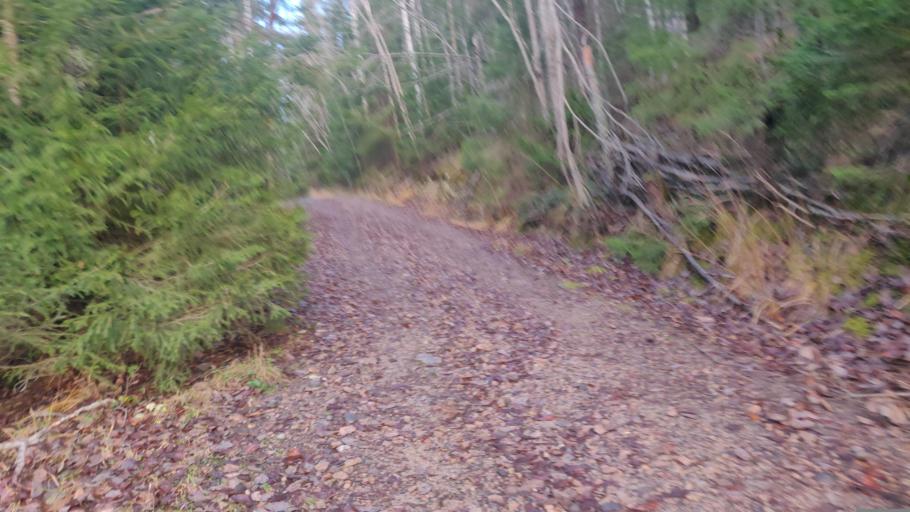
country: SE
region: Vaesternorrland
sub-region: Sundsvalls Kommun
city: Nolby
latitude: 62.3043
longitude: 17.3555
